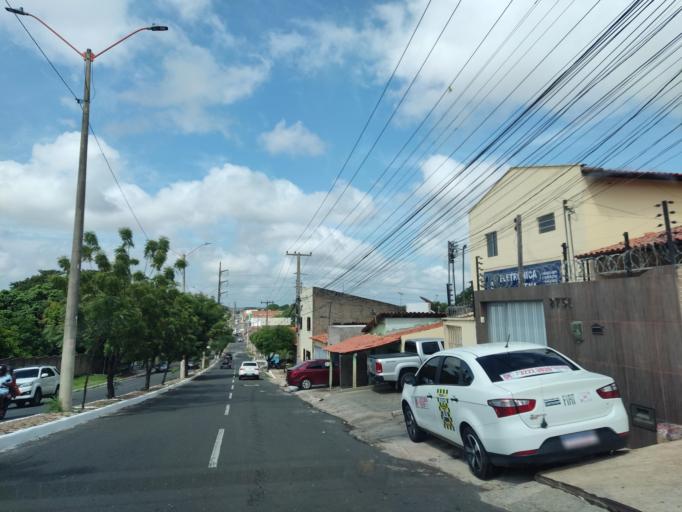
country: BR
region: Piaui
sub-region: Teresina
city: Teresina
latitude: -5.0722
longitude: -42.8079
